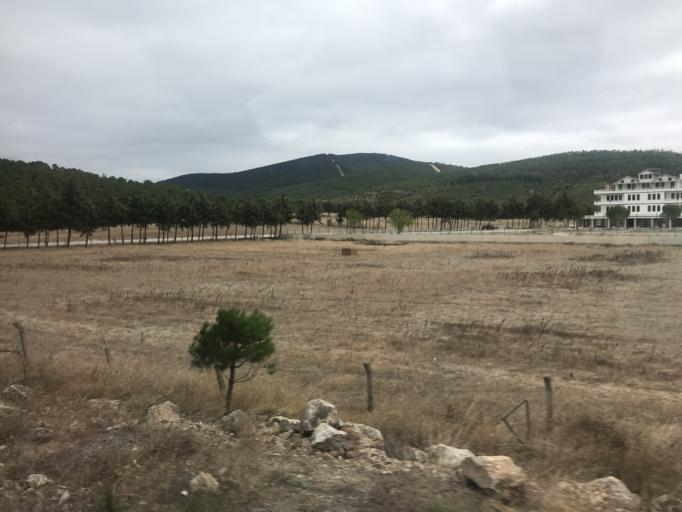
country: TR
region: Balikesir
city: Ergama
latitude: 39.6236
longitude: 27.5897
